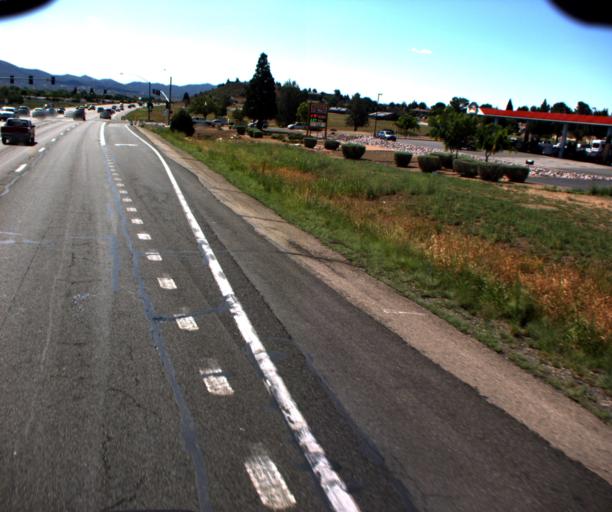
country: US
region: Arizona
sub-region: Yavapai County
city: Dewey-Humboldt
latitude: 34.5626
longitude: -112.2607
